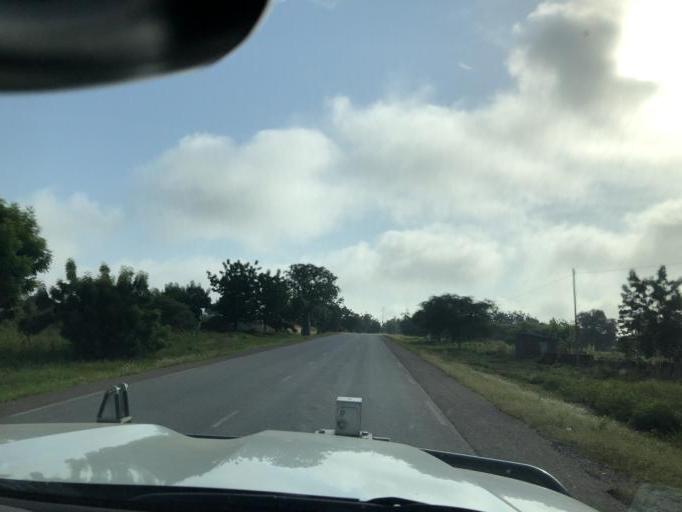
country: CM
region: North Province
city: Pitoa
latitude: 9.4938
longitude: 13.6879
